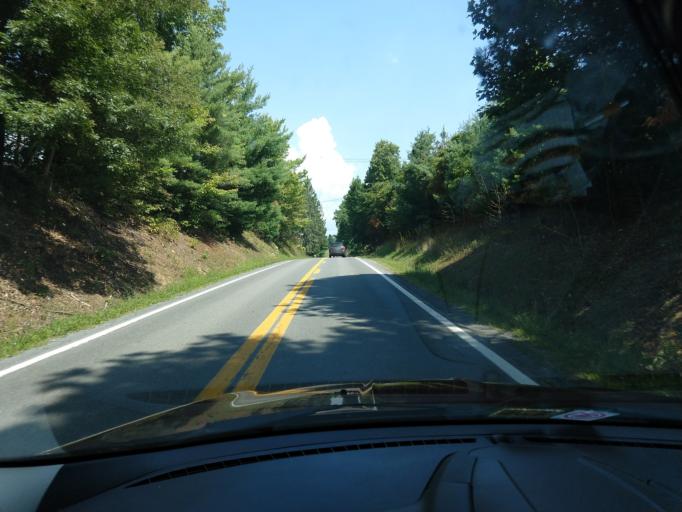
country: US
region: West Virginia
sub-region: Greenbrier County
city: Fairlea
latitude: 37.8370
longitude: -80.5549
